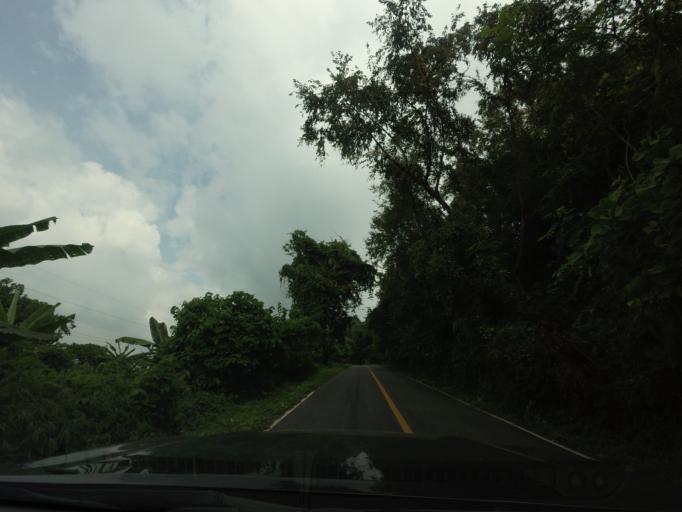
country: TH
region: Nan
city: Pua
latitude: 19.1881
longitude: 101.0219
